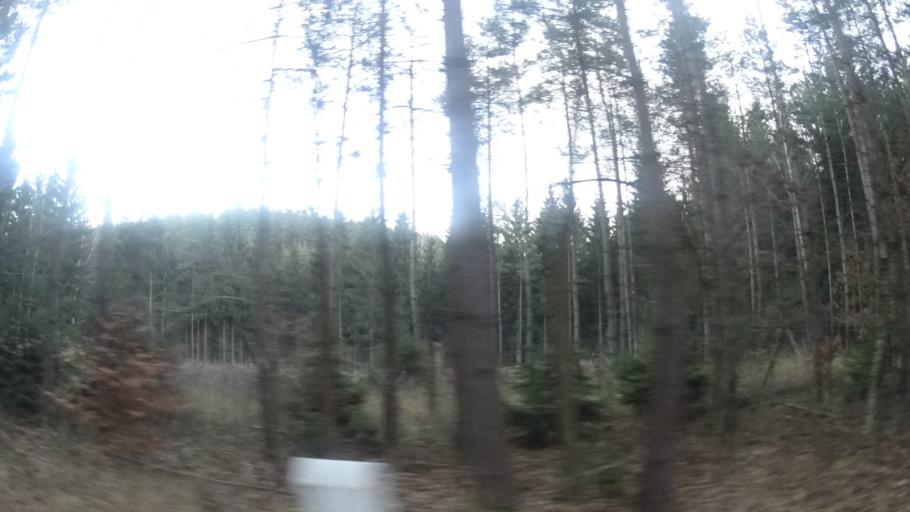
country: DE
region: Thuringia
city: Unterwellenborn
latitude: 50.6747
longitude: 11.4272
